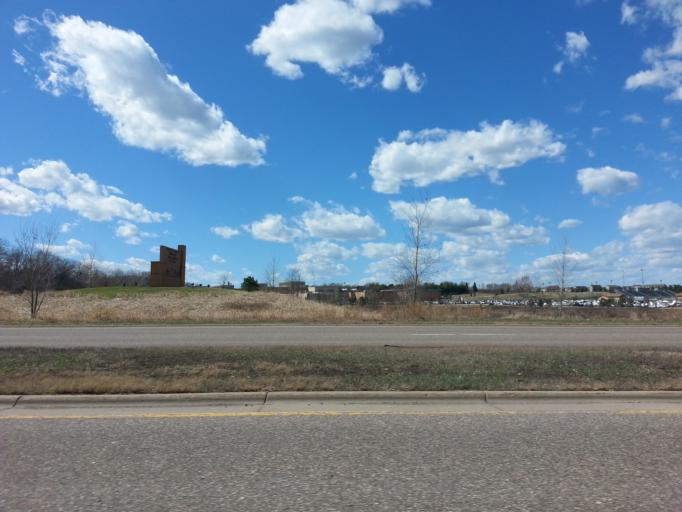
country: US
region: Minnesota
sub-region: Scott County
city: Prior Lake
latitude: 44.7265
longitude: -93.3729
